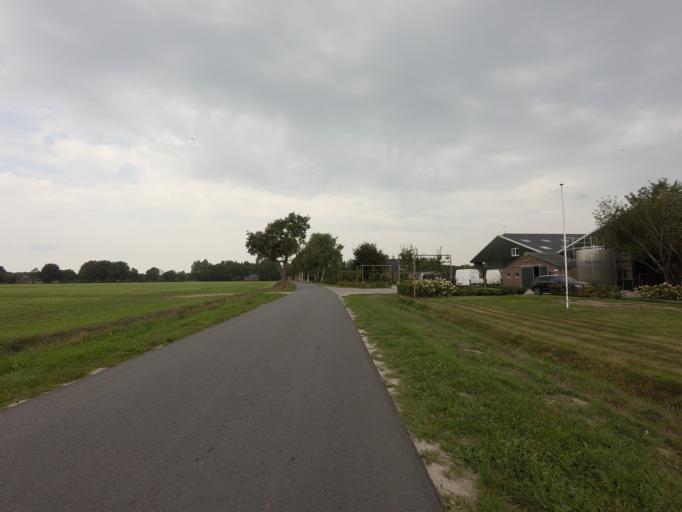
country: NL
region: Drenthe
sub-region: Gemeente Tynaarlo
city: Vries
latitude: 53.0625
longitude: 6.5846
